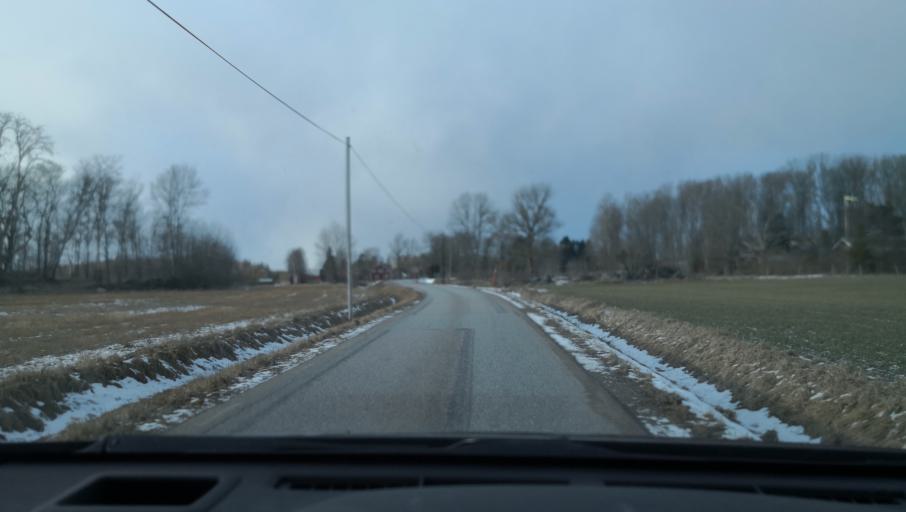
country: SE
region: Uppsala
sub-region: Enkopings Kommun
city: Irsta
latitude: 59.6988
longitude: 16.9435
